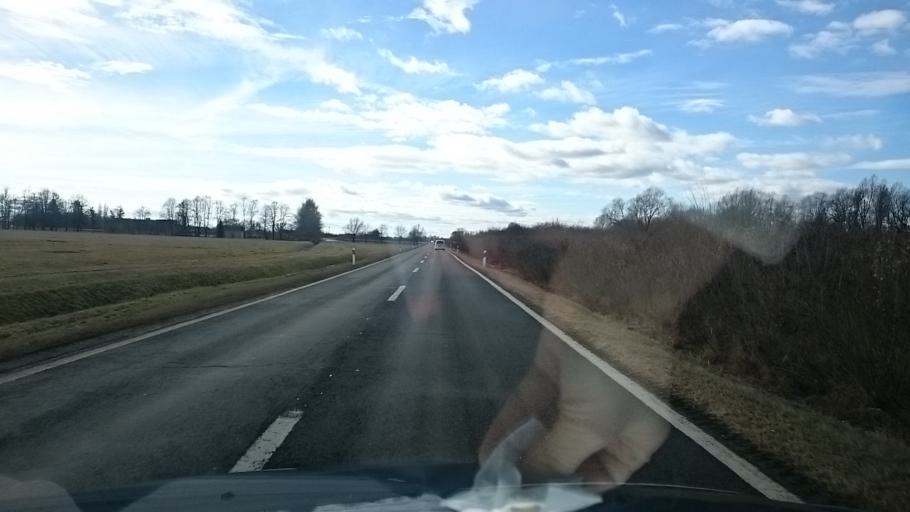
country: HR
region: Sisacko-Moslavacka
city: Novska
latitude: 45.2810
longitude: 16.9231
